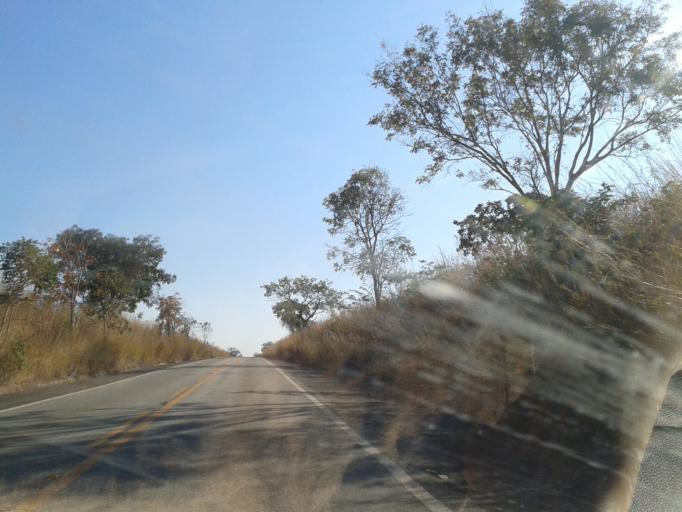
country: BR
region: Goias
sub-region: Mozarlandia
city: Mozarlandia
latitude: -14.9716
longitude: -50.5804
